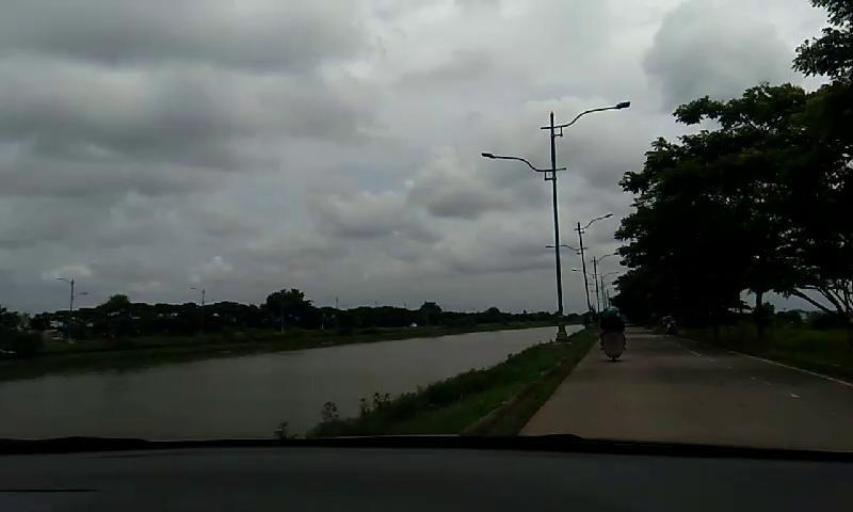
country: ID
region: West Java
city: Bekasi
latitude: -6.1235
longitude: 106.9693
